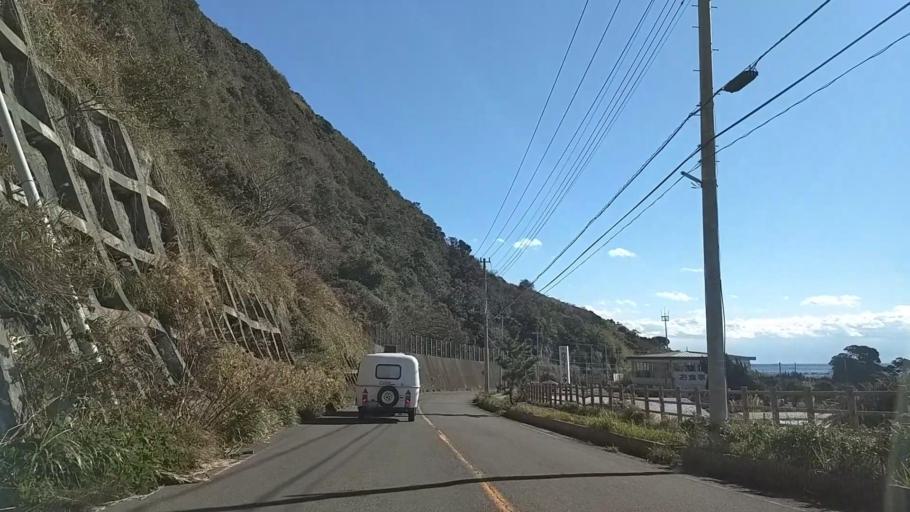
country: JP
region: Chiba
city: Tateyama
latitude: 34.9113
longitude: 139.8282
